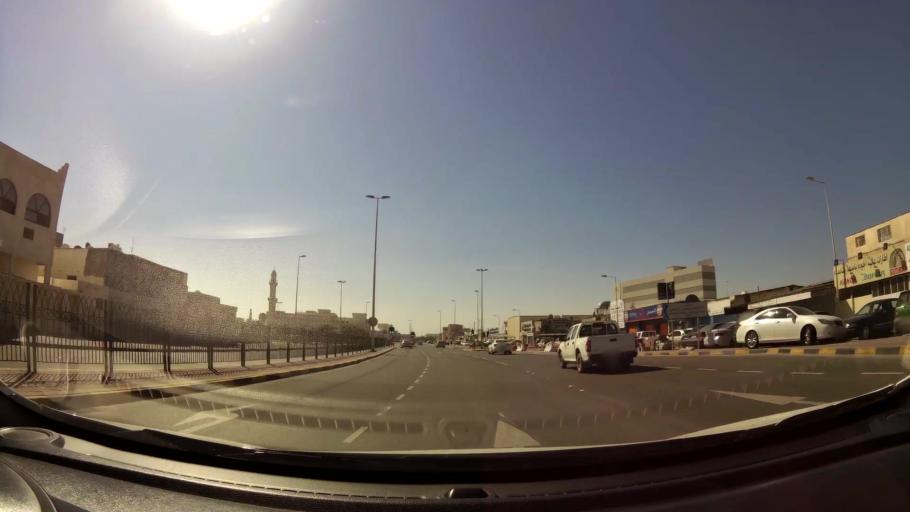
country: BH
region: Muharraq
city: Al Hadd
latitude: 26.2565
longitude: 50.6462
